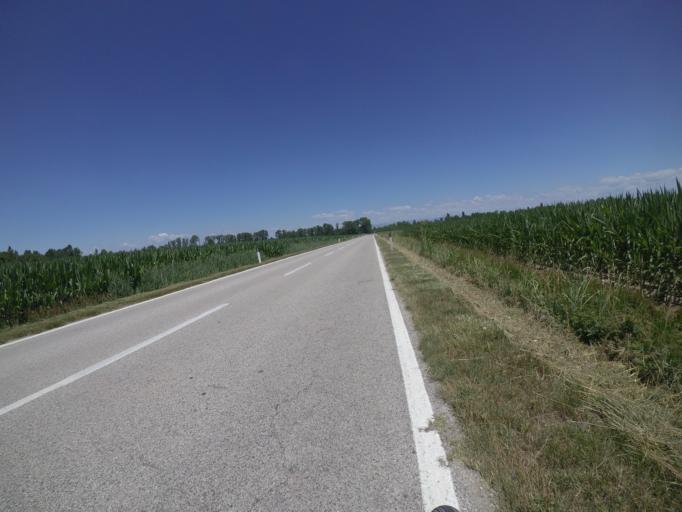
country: IT
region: Friuli Venezia Giulia
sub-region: Provincia di Udine
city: Bertiolo
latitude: 45.9103
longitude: 13.0816
